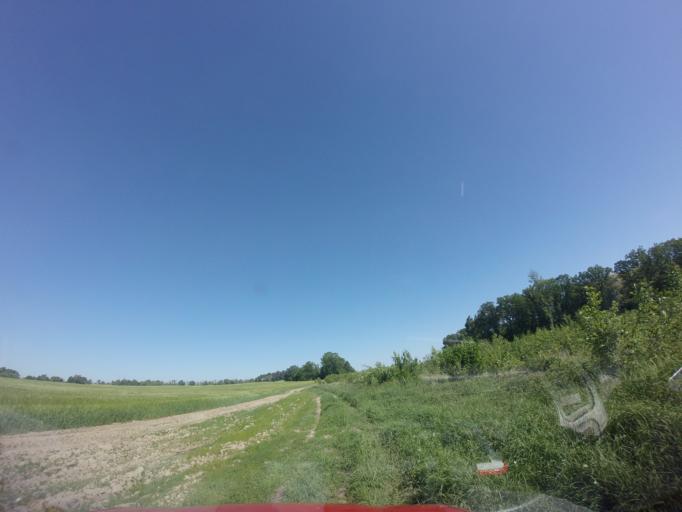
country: PL
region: West Pomeranian Voivodeship
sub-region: Powiat choszczenski
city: Choszczno
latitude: 53.1717
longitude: 15.3529
